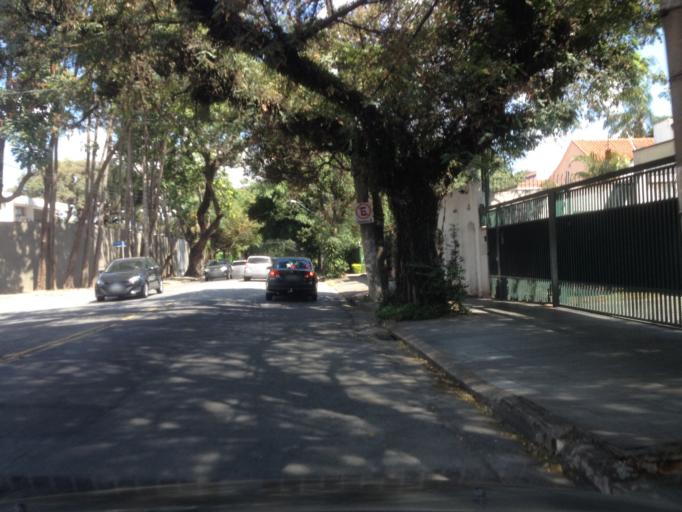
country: BR
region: Sao Paulo
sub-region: Sao Paulo
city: Sao Paulo
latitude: -23.5500
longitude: -46.7067
